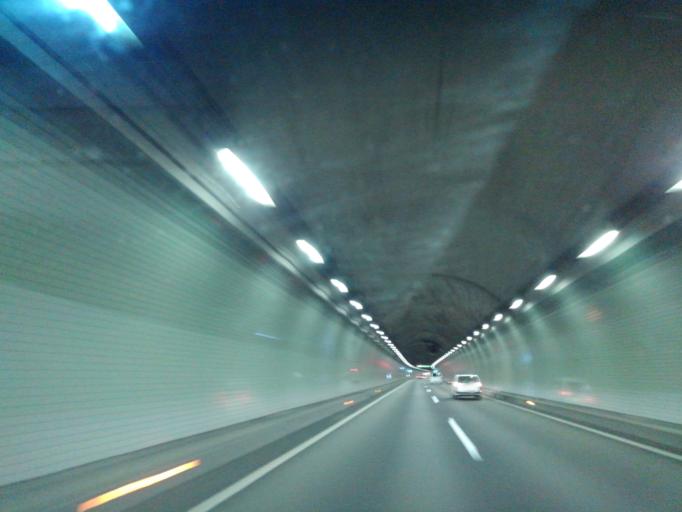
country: JP
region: Tokyo
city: Fussa
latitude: 35.7622
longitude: 139.2872
